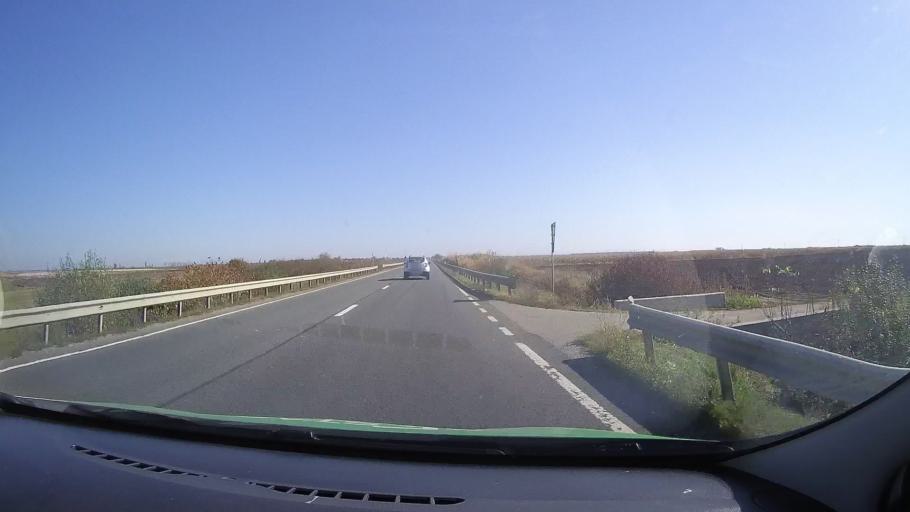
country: RO
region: Satu Mare
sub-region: Comuna Moftinu
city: Moftinu Mic
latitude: 47.6848
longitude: 22.5658
